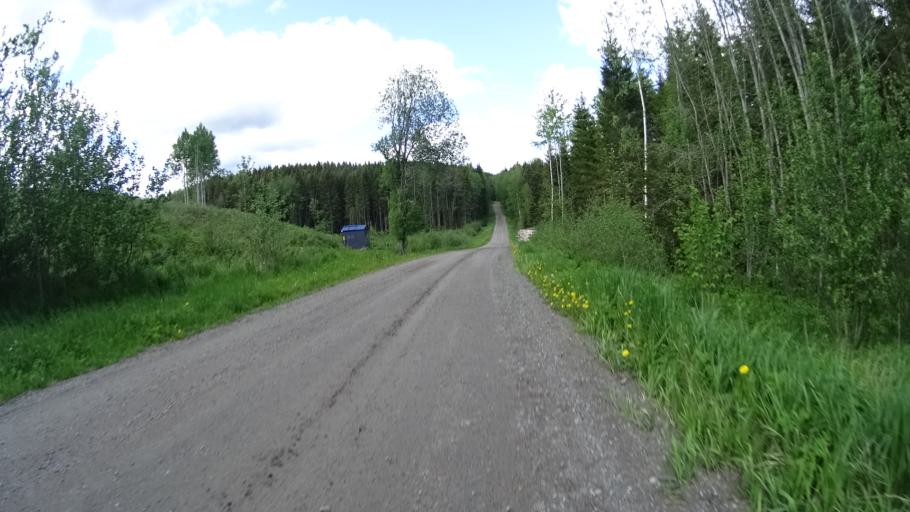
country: FI
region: Uusimaa
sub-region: Raaseporin
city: Pohja
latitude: 60.1619
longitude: 23.6055
